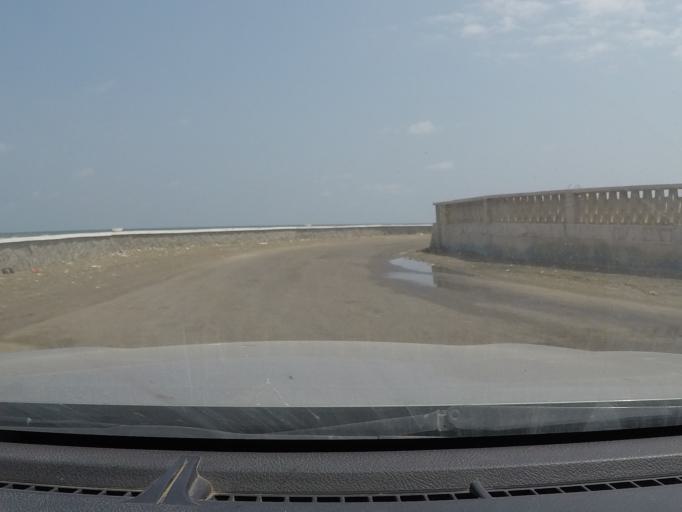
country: YE
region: Aden
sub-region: Khur Maksar
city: Khawr Maksar
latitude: 12.8142
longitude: 45.0429
